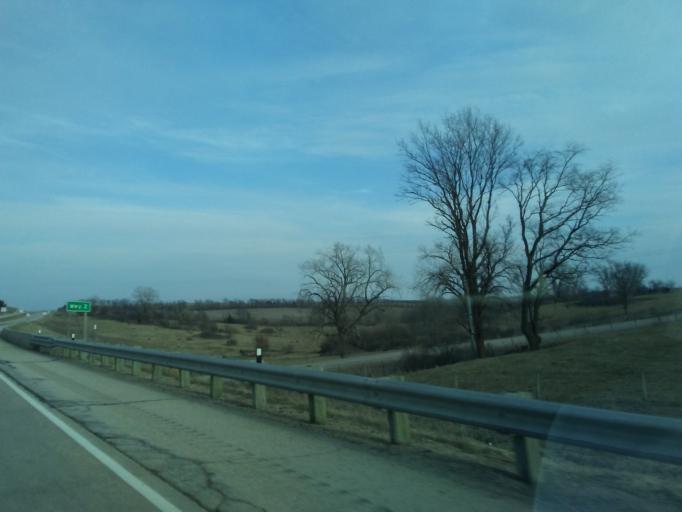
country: US
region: Wisconsin
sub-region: Iowa County
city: Dodgeville
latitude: 42.9673
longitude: -90.0940
